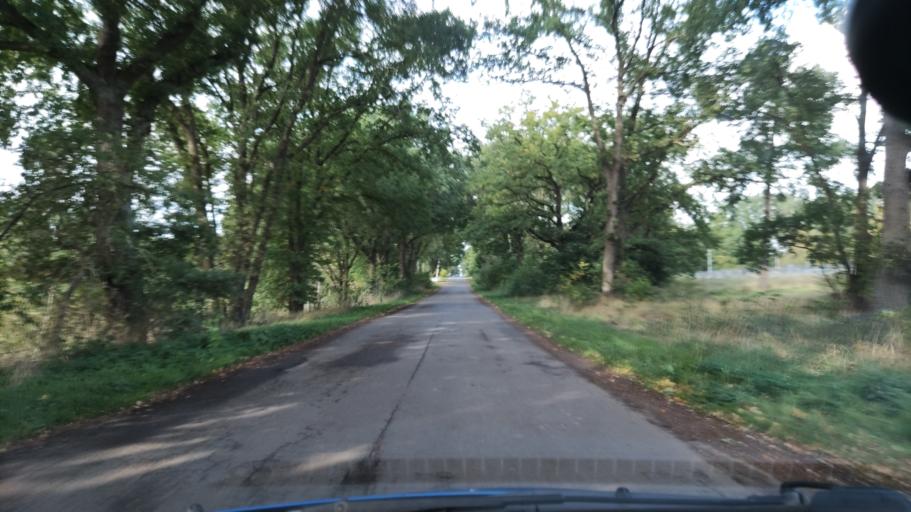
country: DE
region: Lower Saxony
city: Deutsch Evern
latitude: 53.2019
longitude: 10.4505
